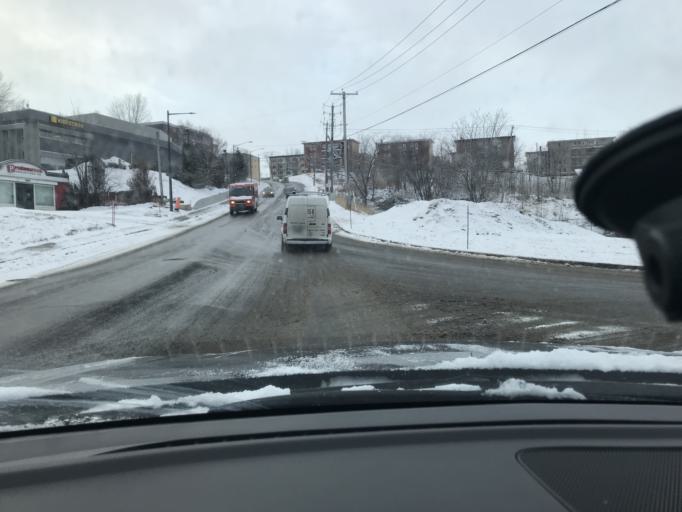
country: CA
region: Quebec
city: Quebec
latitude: 46.7936
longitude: -71.2726
